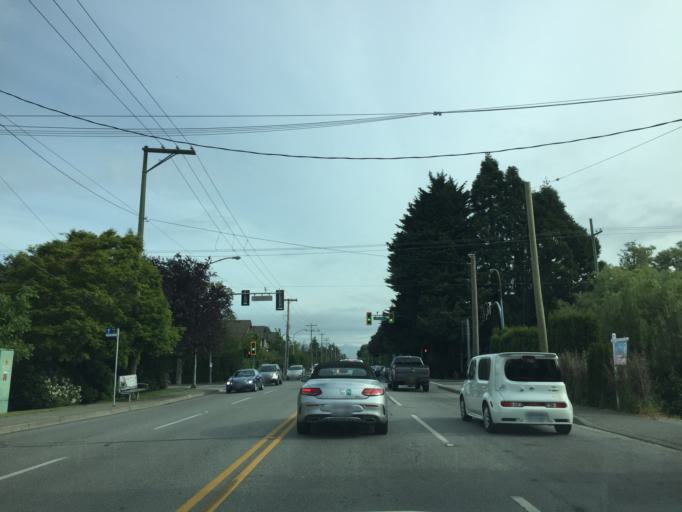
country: CA
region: British Columbia
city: Richmond
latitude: 49.1405
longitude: -123.1589
